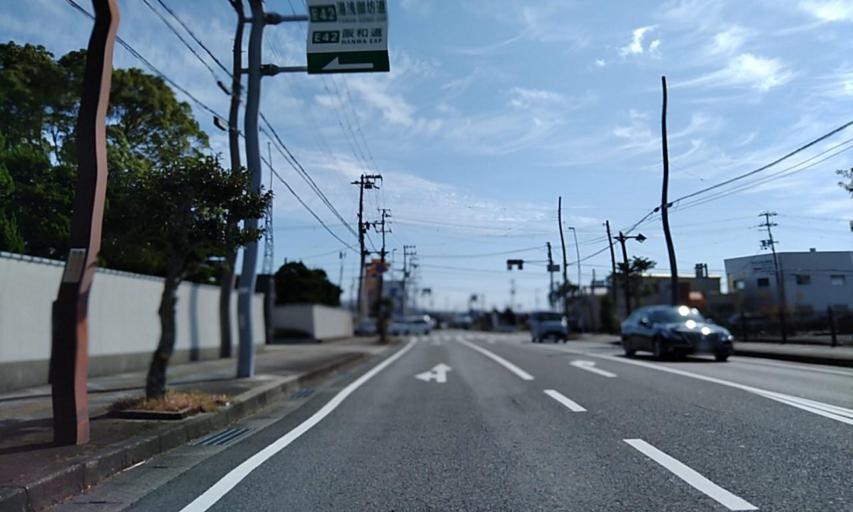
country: JP
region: Wakayama
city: Gobo
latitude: 33.9015
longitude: 135.1617
